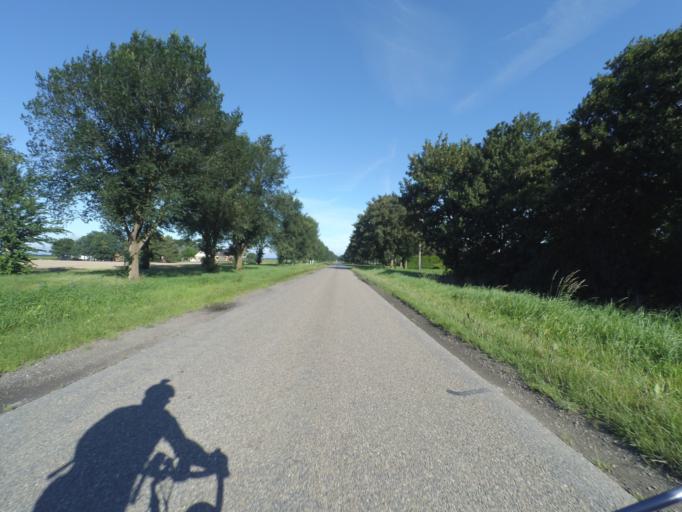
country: NL
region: Flevoland
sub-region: Gemeente Zeewolde
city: Zeewolde
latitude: 52.3843
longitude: 5.4962
